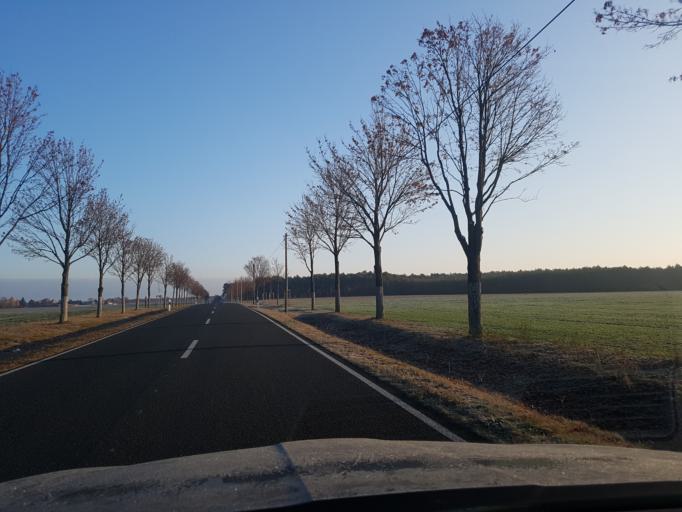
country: DE
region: Brandenburg
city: Herzberg
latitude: 51.6622
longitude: 13.2850
